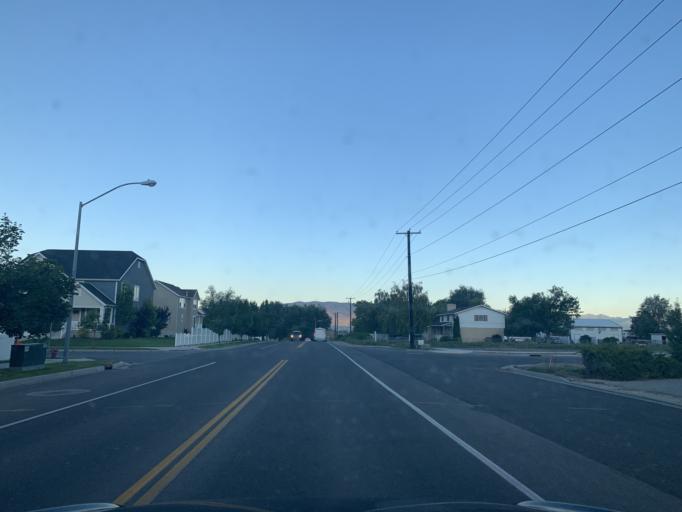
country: US
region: Utah
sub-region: Utah County
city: Orem
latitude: 40.2608
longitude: -111.7136
